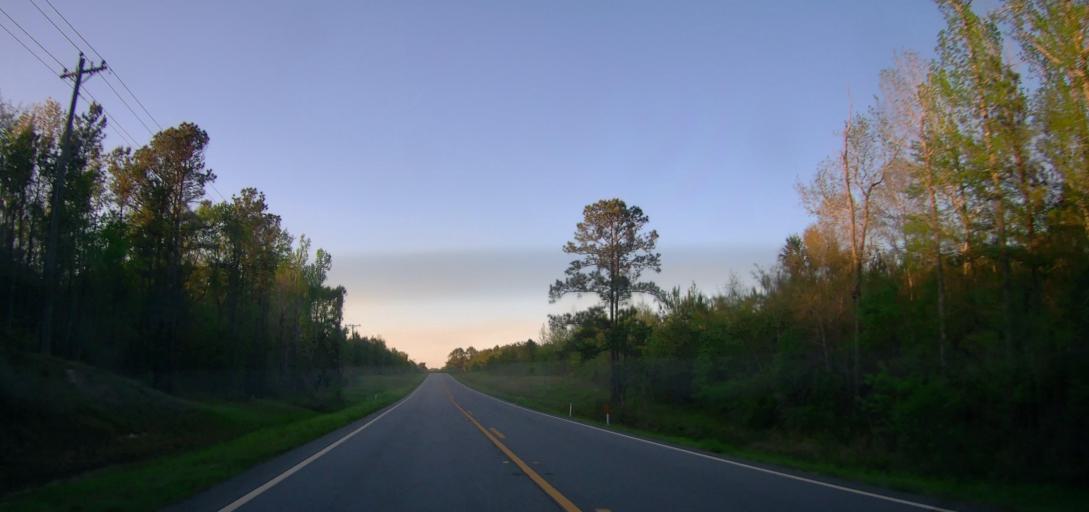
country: US
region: Georgia
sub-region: Talbot County
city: Talbotton
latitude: 32.5591
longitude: -84.5690
